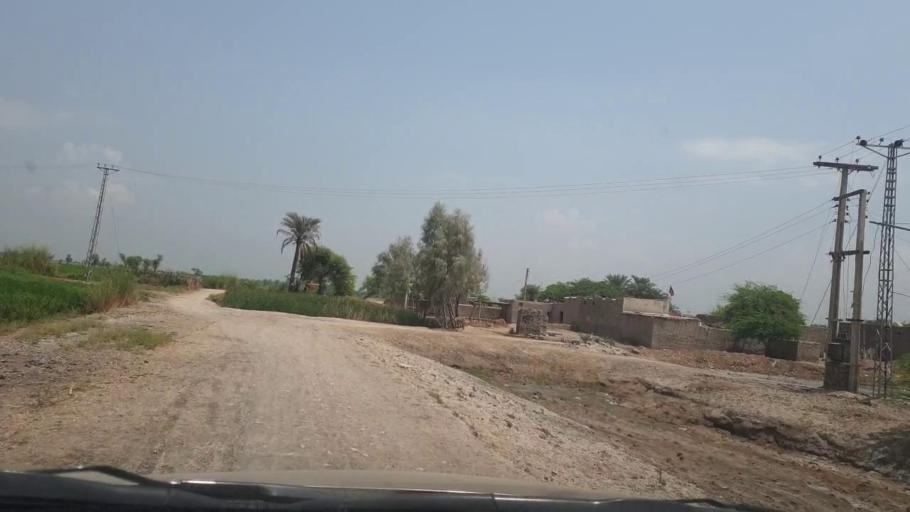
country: PK
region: Sindh
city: Ratodero
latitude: 27.7564
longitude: 68.2945
